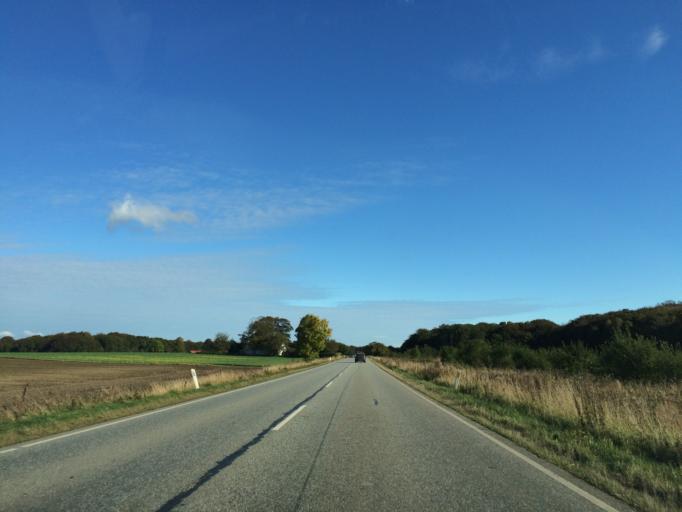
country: DK
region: Central Jutland
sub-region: Randers Kommune
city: Langa
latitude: 56.3893
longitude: 9.9673
